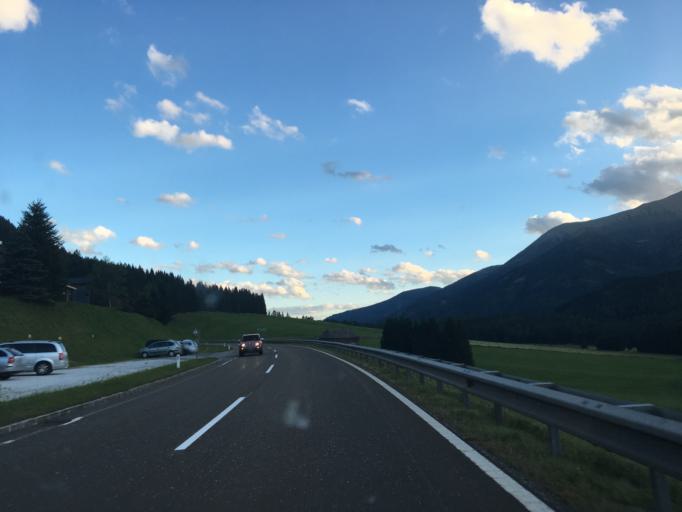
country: AT
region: Styria
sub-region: Politischer Bezirk Murtal
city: Hohentauern
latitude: 47.4247
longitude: 14.4626
